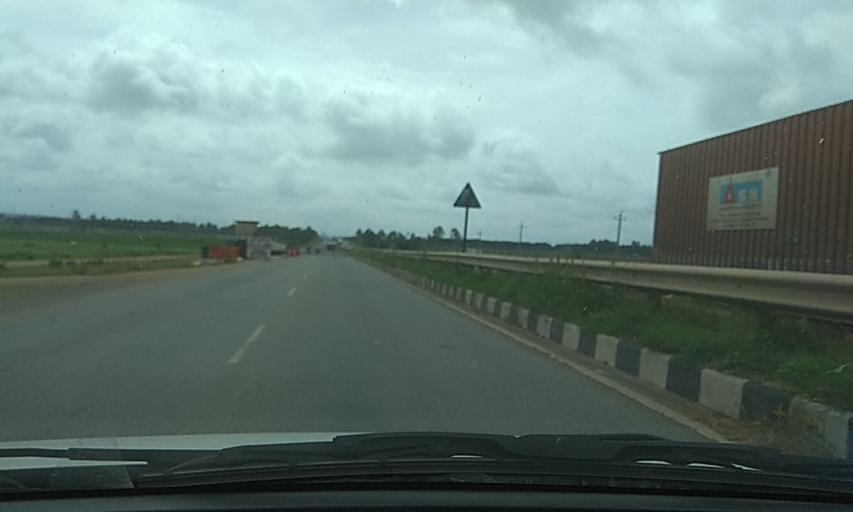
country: IN
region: Karnataka
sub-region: Davanagere
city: Harihar
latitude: 14.4500
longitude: 75.8791
